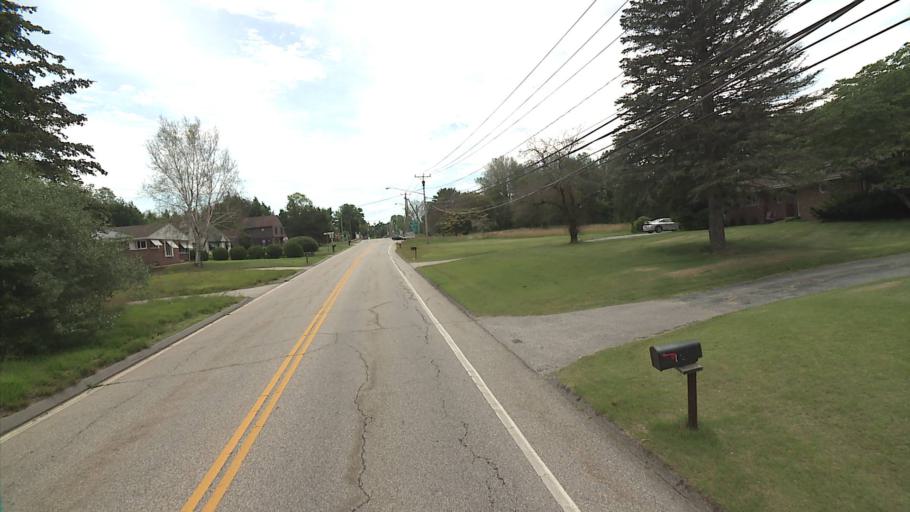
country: US
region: Connecticut
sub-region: New London County
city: Jewett City
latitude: 41.5927
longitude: -71.9762
